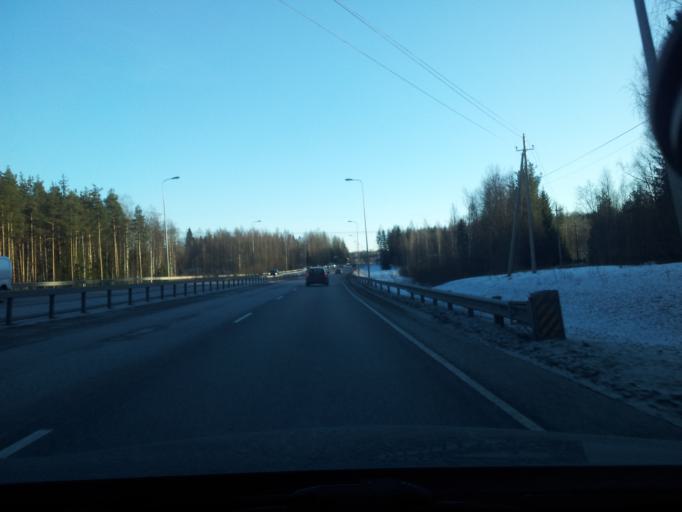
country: FI
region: Uusimaa
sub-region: Helsinki
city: Vihti
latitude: 60.3205
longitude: 24.3426
